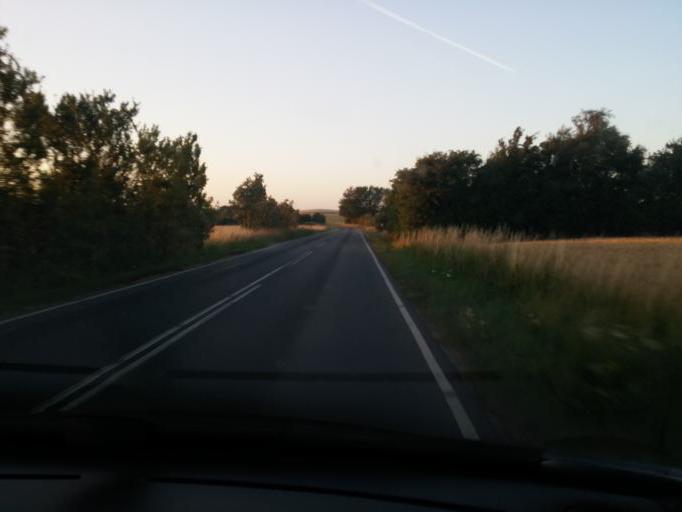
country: DK
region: South Denmark
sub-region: Langeland Kommune
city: Rudkobing
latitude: 54.8719
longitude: 10.7330
